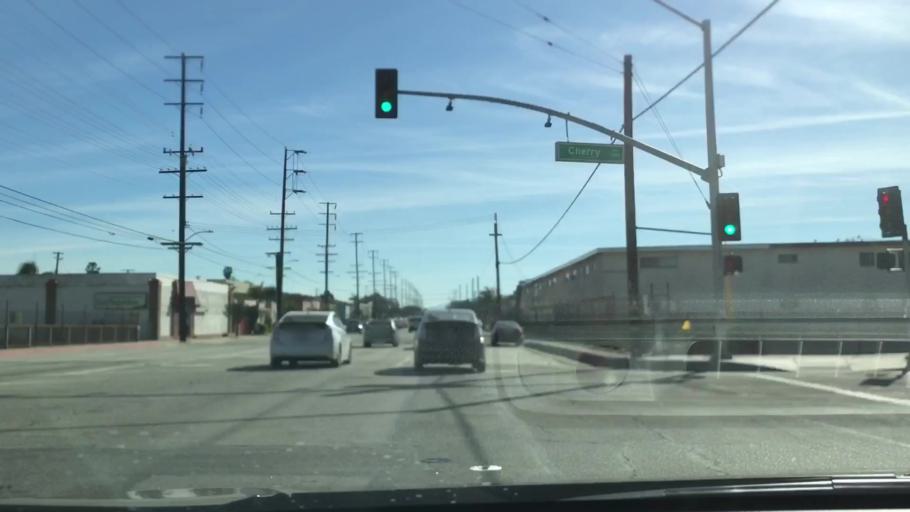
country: US
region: California
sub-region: Los Angeles County
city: Alondra Park
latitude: 33.8801
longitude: -118.3266
